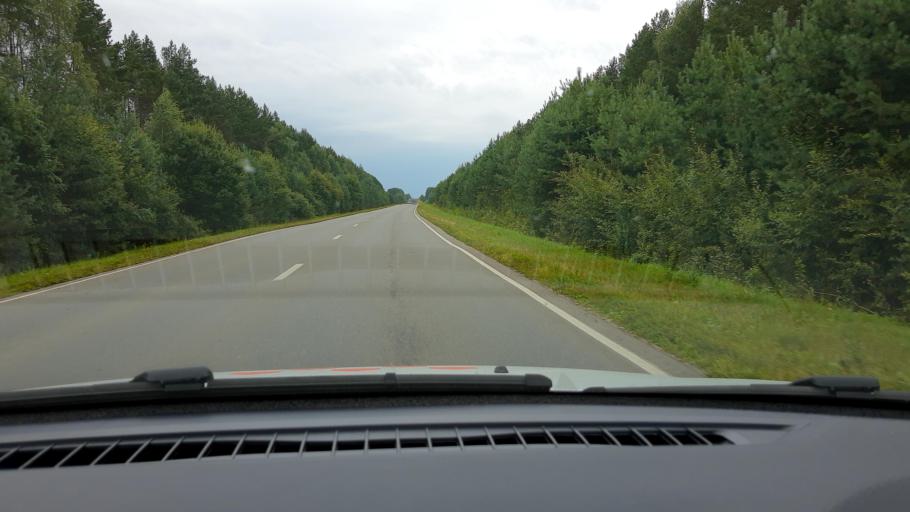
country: RU
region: Nizjnij Novgorod
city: Vyyezdnoye
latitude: 55.1668
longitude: 43.5901
